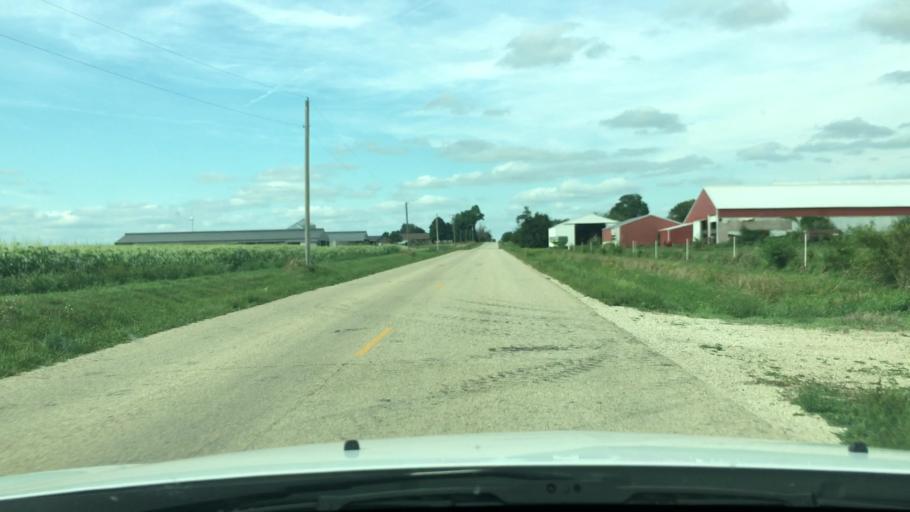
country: US
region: Illinois
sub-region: DeKalb County
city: Malta
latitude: 41.8714
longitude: -88.9615
